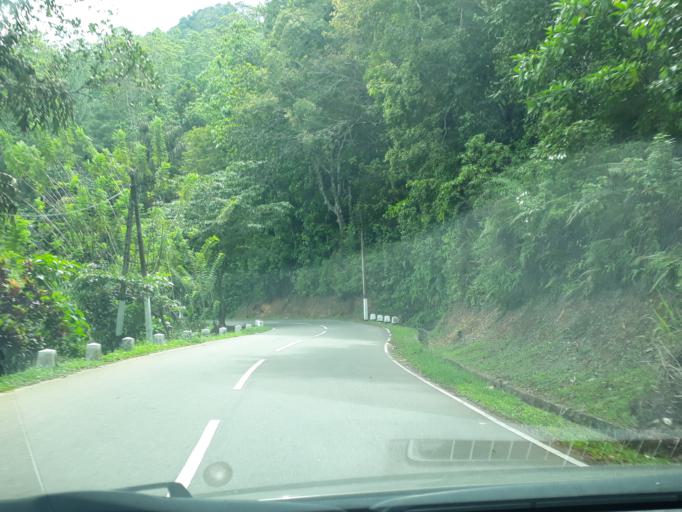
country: LK
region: Southern
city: Weligama
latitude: 6.3130
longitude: 80.5436
